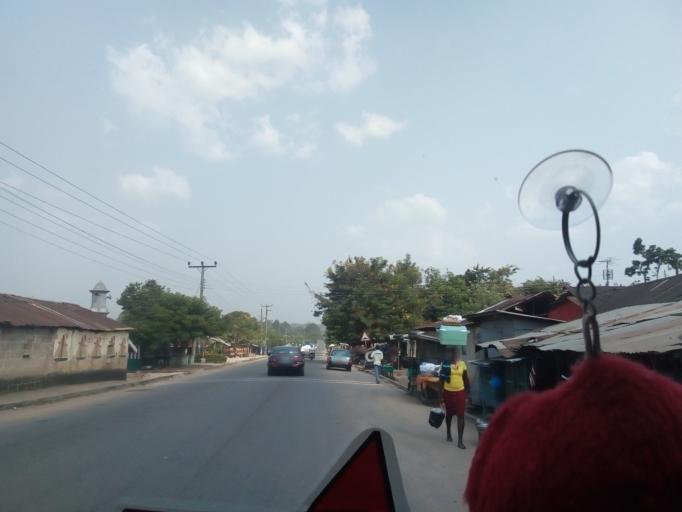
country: GH
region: Eastern
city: Suhum
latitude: 6.0426
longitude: -0.4341
